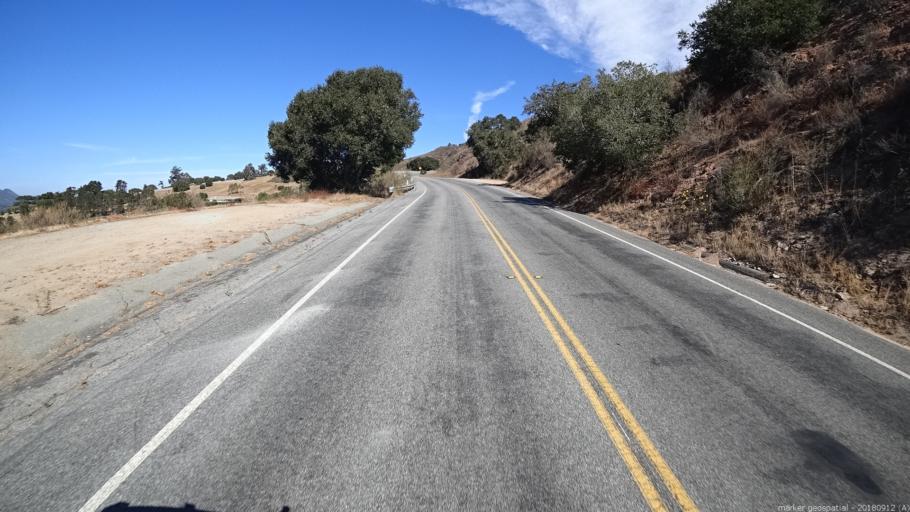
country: US
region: California
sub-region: Monterey County
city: Carmel Valley Village
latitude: 36.5126
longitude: -121.7554
